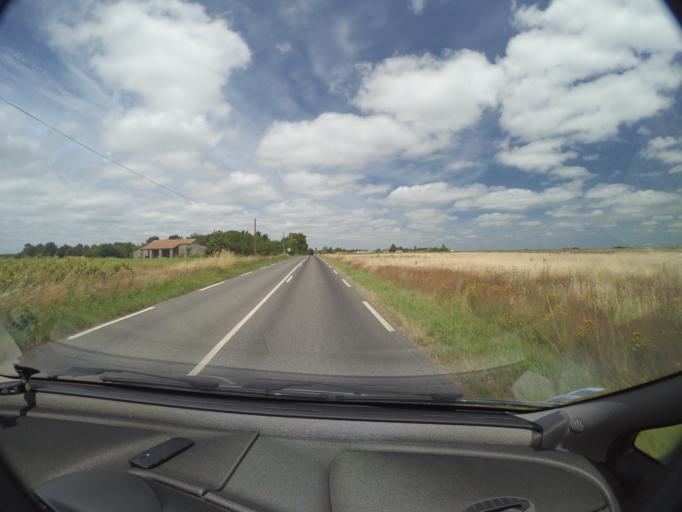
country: FR
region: Pays de la Loire
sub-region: Departement de la Loire-Atlantique
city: Gorges
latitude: 47.1105
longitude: -1.2956
